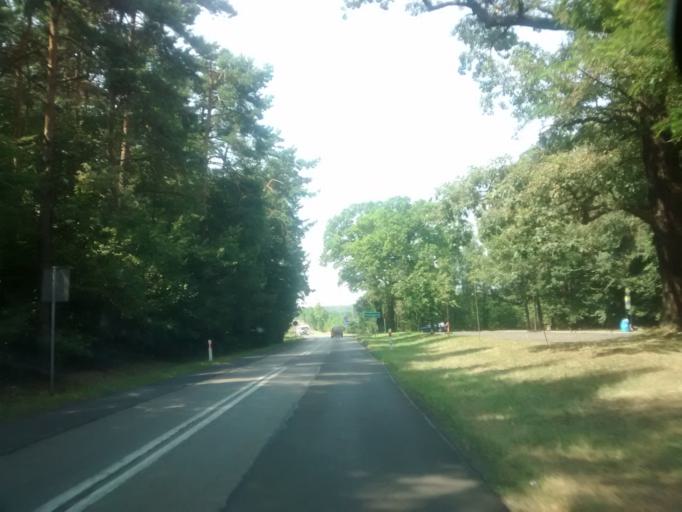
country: PL
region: Silesian Voivodeship
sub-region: Powiat czestochowski
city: Olsztyn
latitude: 50.7457
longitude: 19.3219
